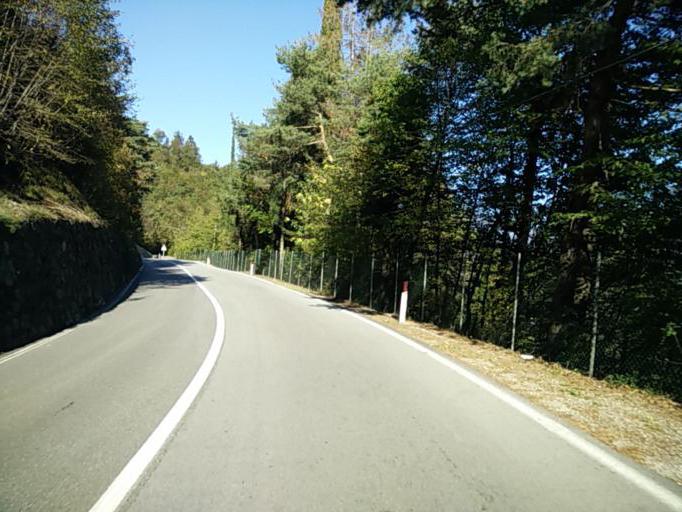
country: IT
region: Lombardy
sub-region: Provincia di Brescia
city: Anfo
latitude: 45.7948
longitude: 10.5012
